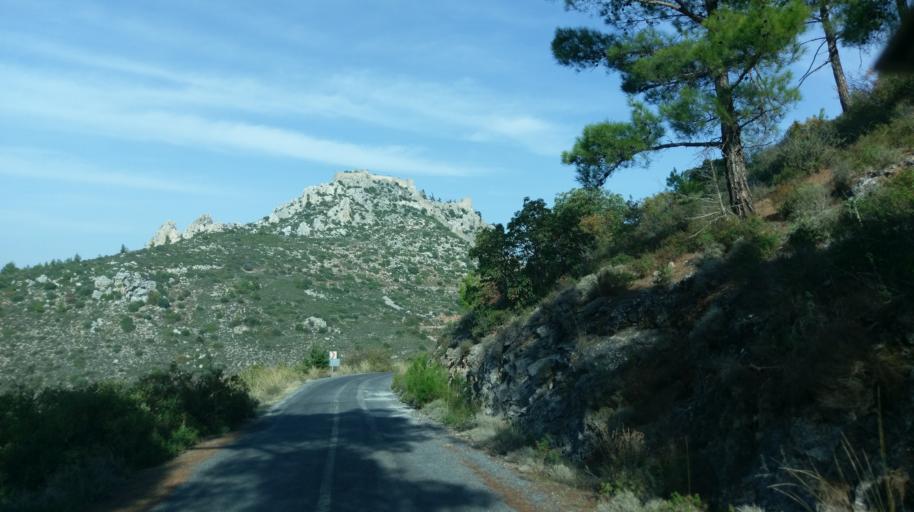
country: CY
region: Keryneia
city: Kyrenia
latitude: 35.3076
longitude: 33.2766
